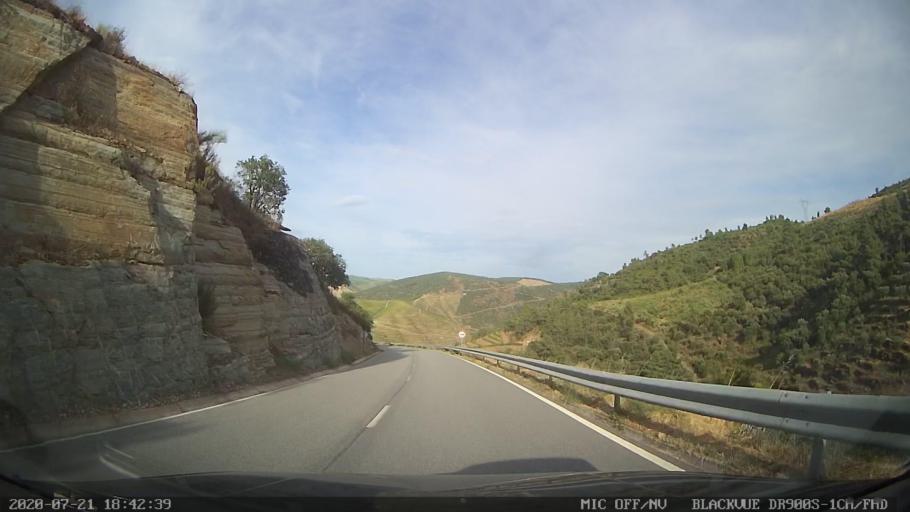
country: PT
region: Viseu
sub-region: Sao Joao da Pesqueira
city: Sao Joao da Pesqueira
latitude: 41.1108
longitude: -7.4655
